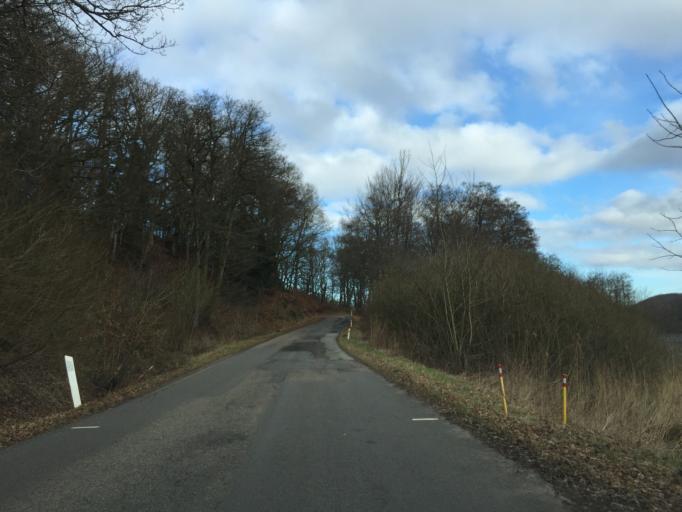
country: DK
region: Central Jutland
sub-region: Viborg Kommune
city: Viborg
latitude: 56.3824
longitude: 9.3324
